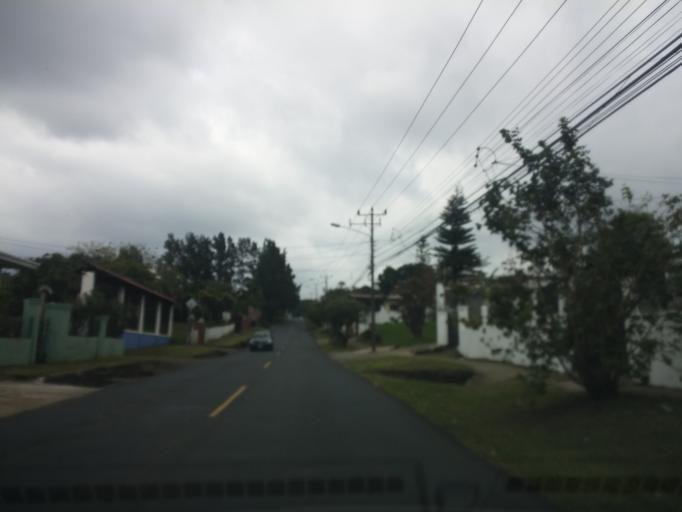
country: CR
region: Heredia
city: Llorente
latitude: 10.0100
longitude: -84.1521
